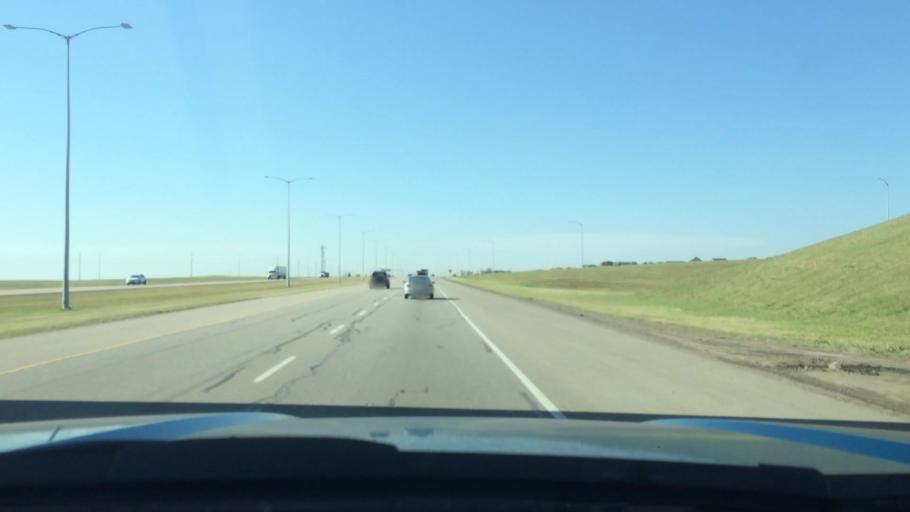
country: CA
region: Alberta
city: Chestermere
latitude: 51.1366
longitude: -113.9216
